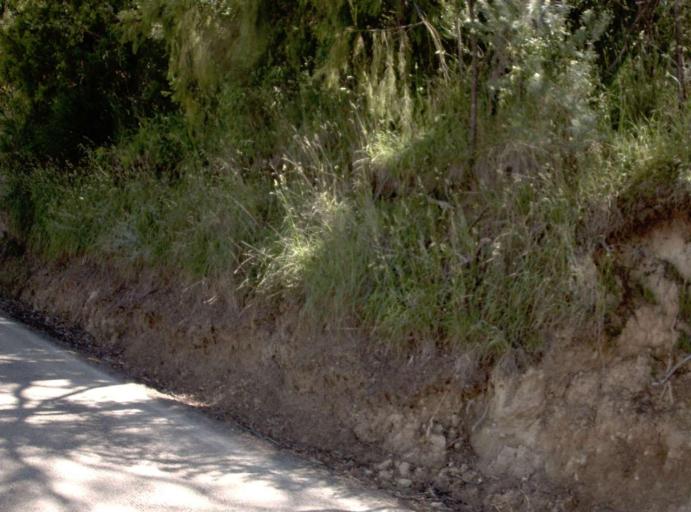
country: AU
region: Victoria
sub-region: East Gippsland
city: Lakes Entrance
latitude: -37.4579
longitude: 148.1956
